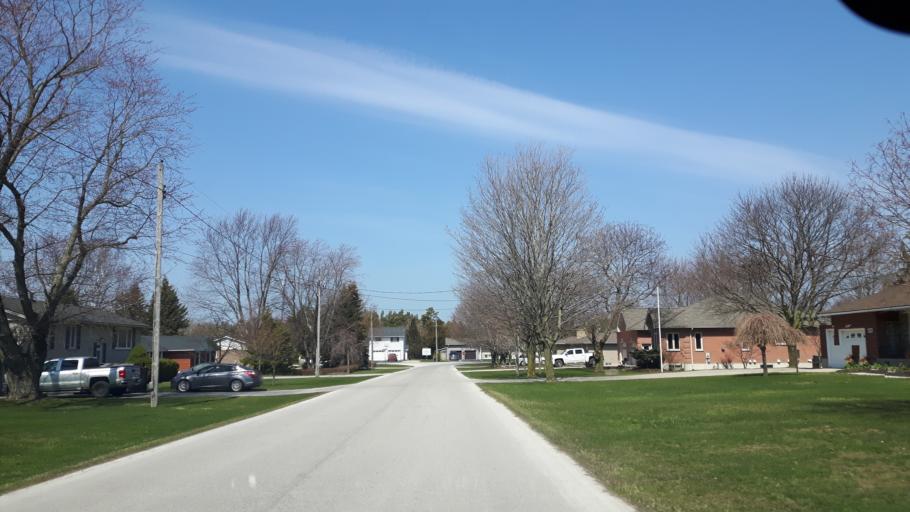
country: CA
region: Ontario
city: Goderich
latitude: 43.7258
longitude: -81.6855
